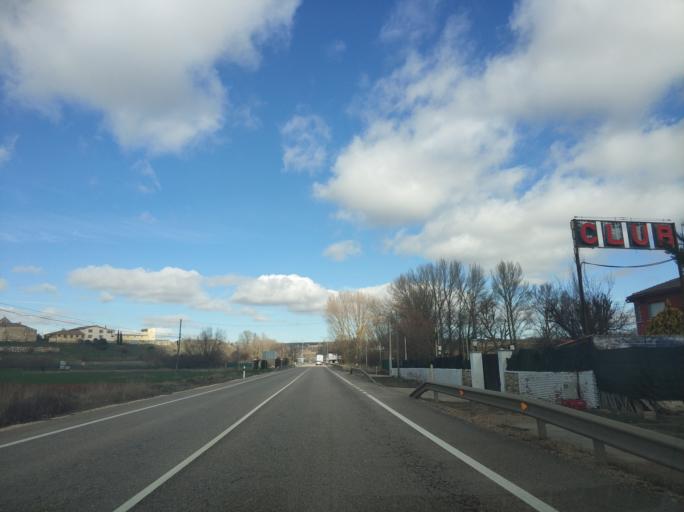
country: ES
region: Castille and Leon
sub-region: Provincia de Burgos
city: Saldana de Burgos
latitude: 42.2578
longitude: -3.6932
